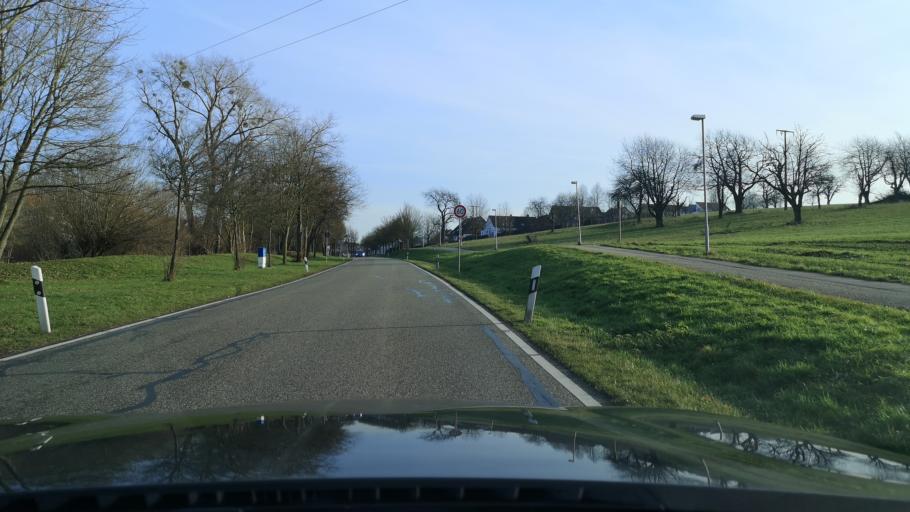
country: DE
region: Baden-Wuerttemberg
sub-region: Karlsruhe Region
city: Ettlingen
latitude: 48.9492
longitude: 8.4743
